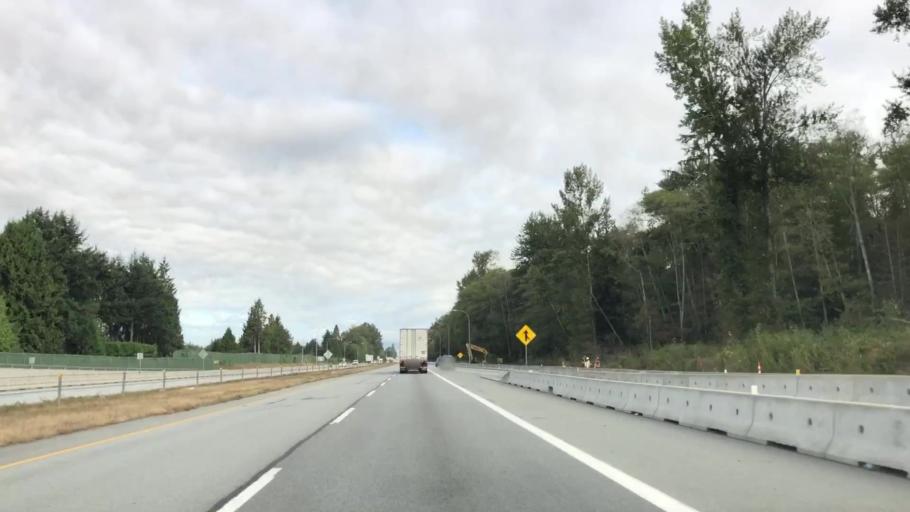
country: CA
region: British Columbia
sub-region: Greater Vancouver Regional District
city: White Rock
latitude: 49.0321
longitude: -122.7702
